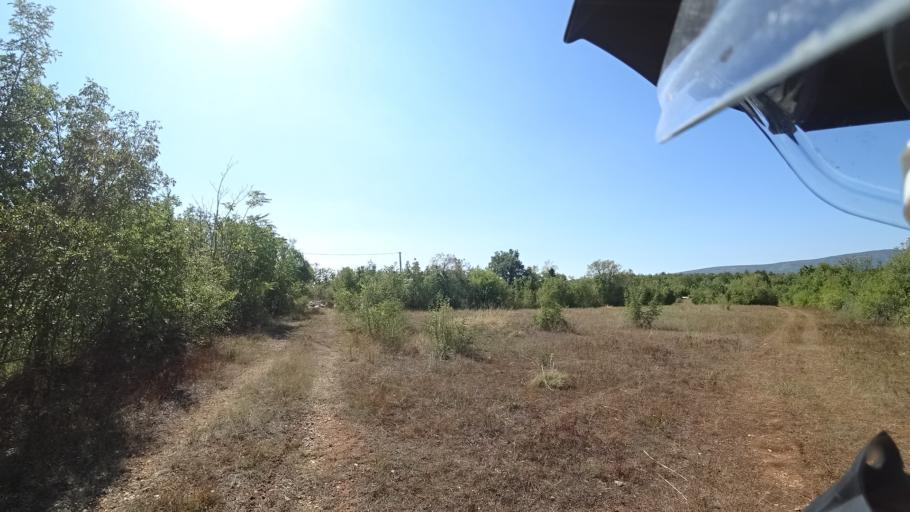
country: HR
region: Sibensko-Kniniska
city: Drnis
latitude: 43.8446
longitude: 16.2853
